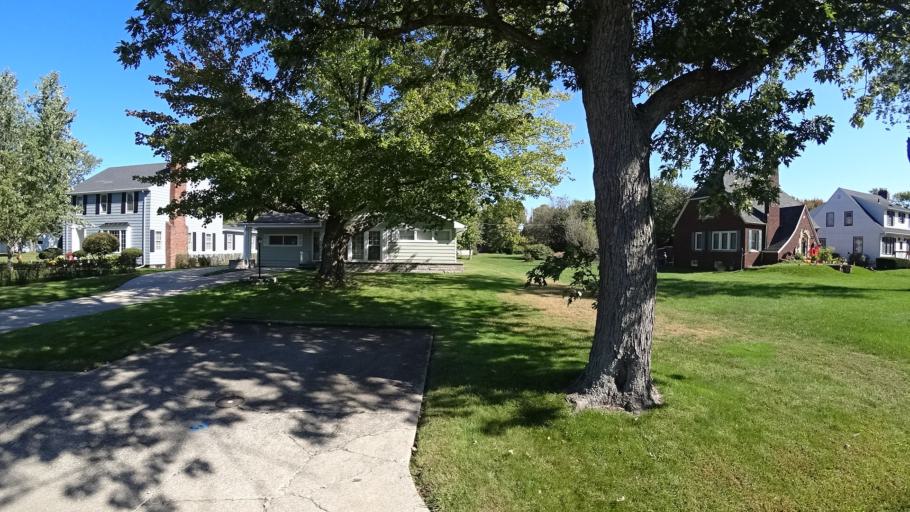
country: US
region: Indiana
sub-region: LaPorte County
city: Michigan City
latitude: 41.6921
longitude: -86.8924
